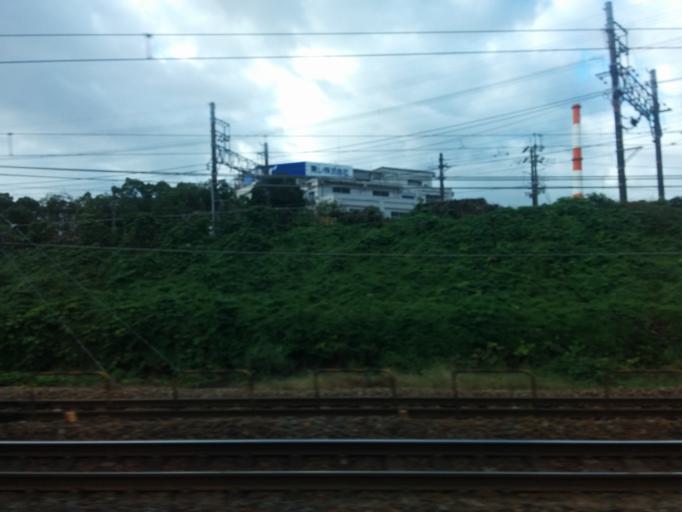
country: JP
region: Shiga Prefecture
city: Otsu-shi
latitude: 34.9808
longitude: 135.8967
